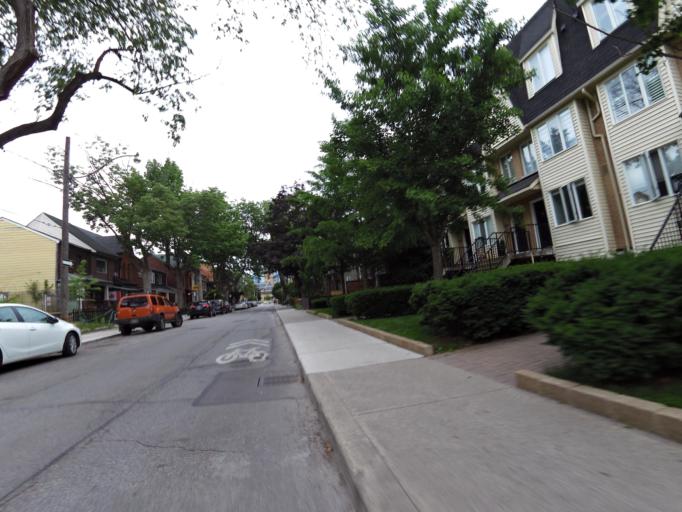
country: CA
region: Ontario
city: Toronto
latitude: 43.6443
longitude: -79.4075
